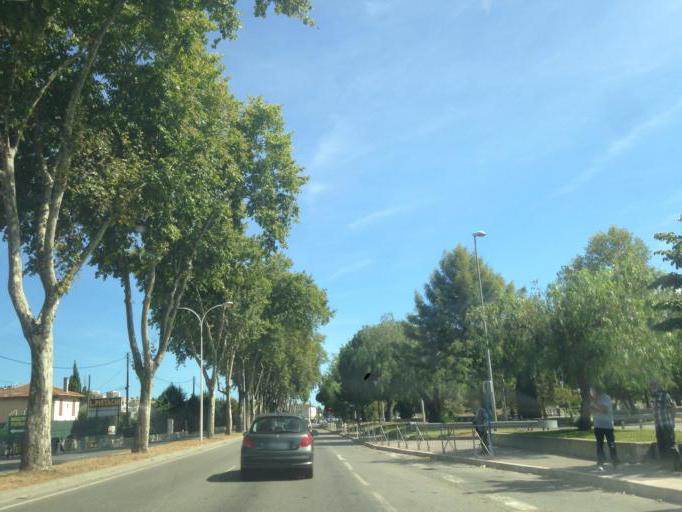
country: FR
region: Provence-Alpes-Cote d'Azur
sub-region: Departement des Alpes-Maritimes
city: Saint-Laurent-du-Var
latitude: 43.6931
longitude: 7.1941
